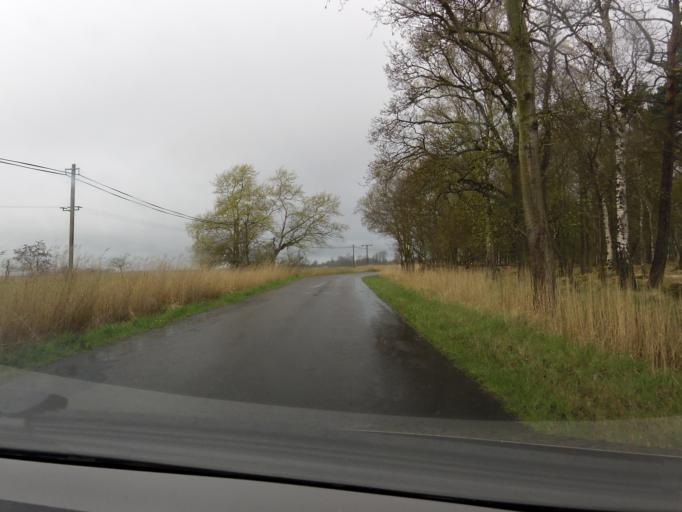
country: DE
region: Mecklenburg-Vorpommern
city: Zingst
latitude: 54.4199
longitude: 12.7472
